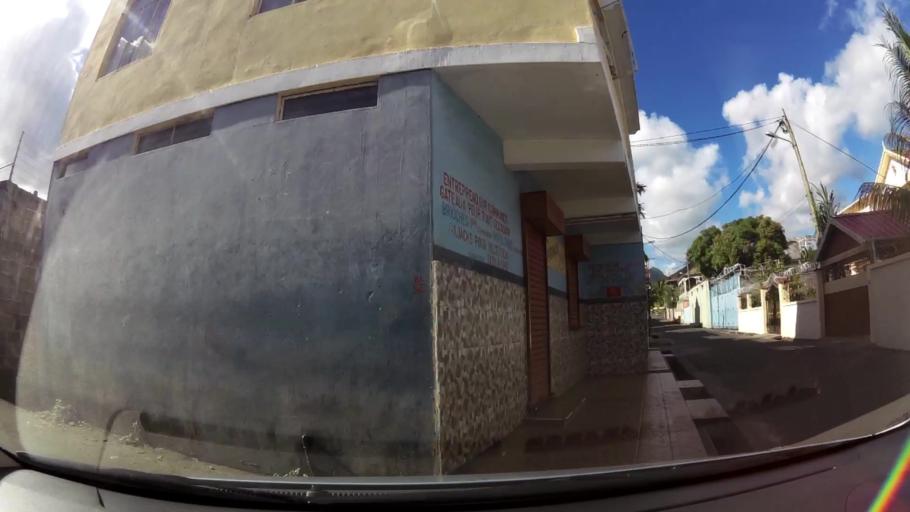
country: MU
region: Pamplemousses
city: Le Hochet
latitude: -20.1476
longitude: 57.5181
